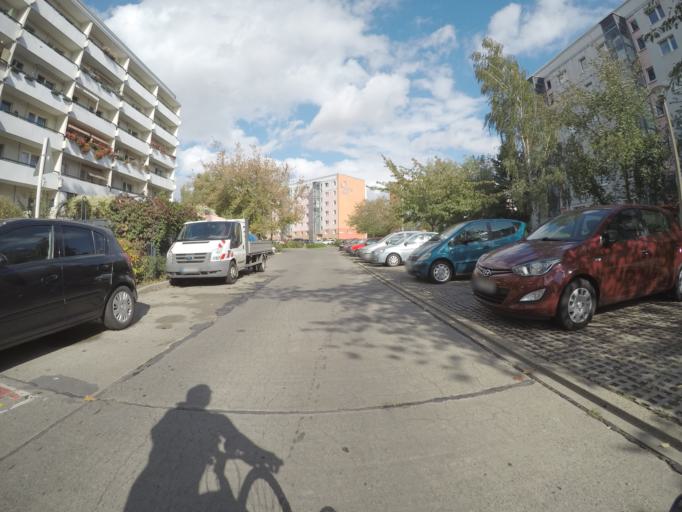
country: DE
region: Berlin
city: Falkenberg
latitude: 52.5666
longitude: 13.5560
